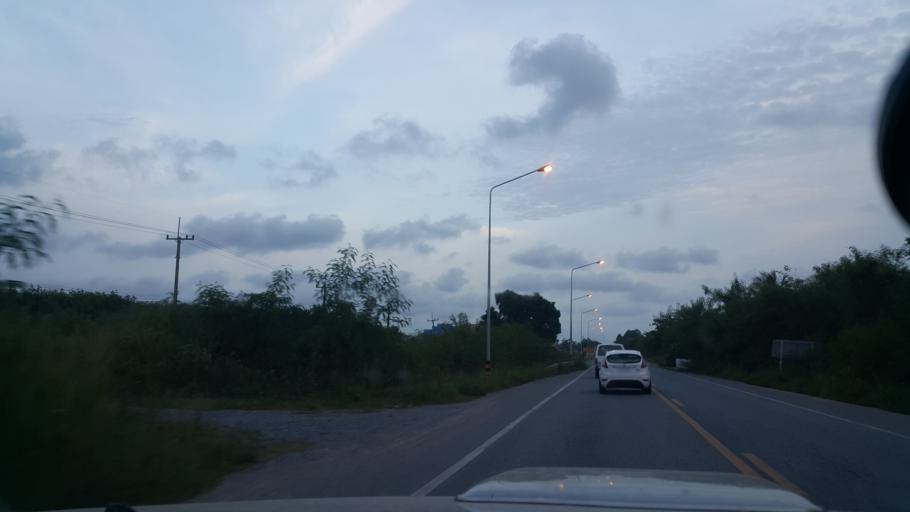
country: TH
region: Rayong
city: Ban Chang
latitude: 12.7161
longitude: 100.9974
